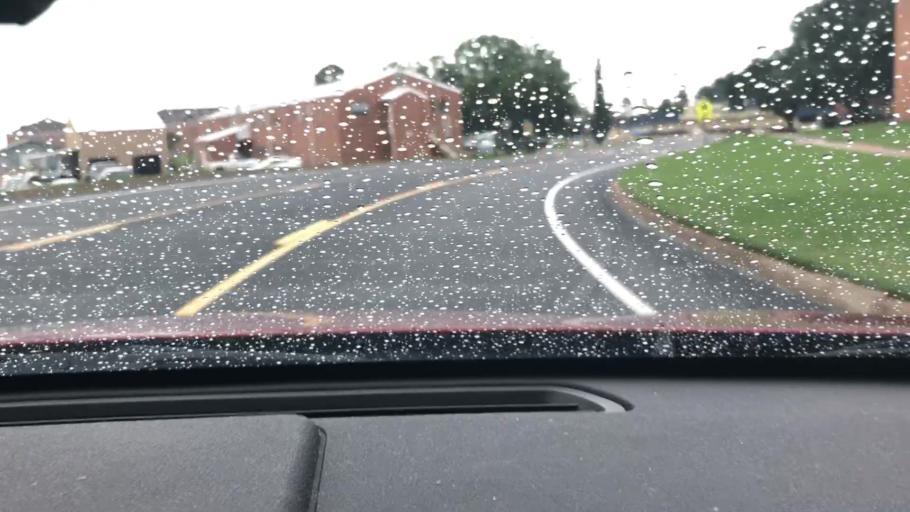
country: US
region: Arkansas
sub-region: Columbia County
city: Magnolia
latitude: 33.2925
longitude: -93.2374
